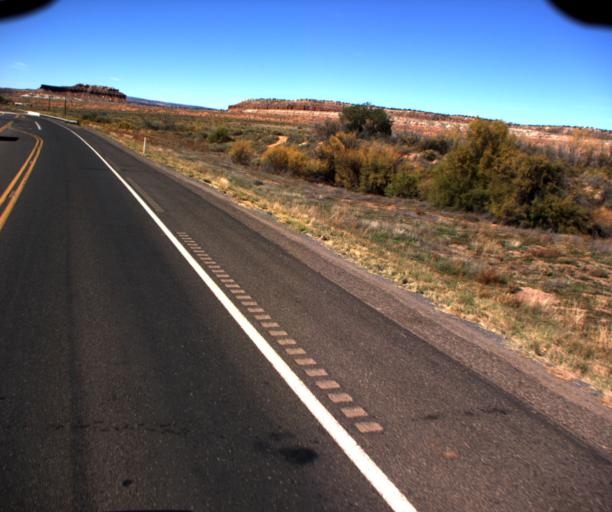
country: US
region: Arizona
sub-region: Coconino County
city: Fredonia
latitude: 36.9457
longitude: -112.5340
